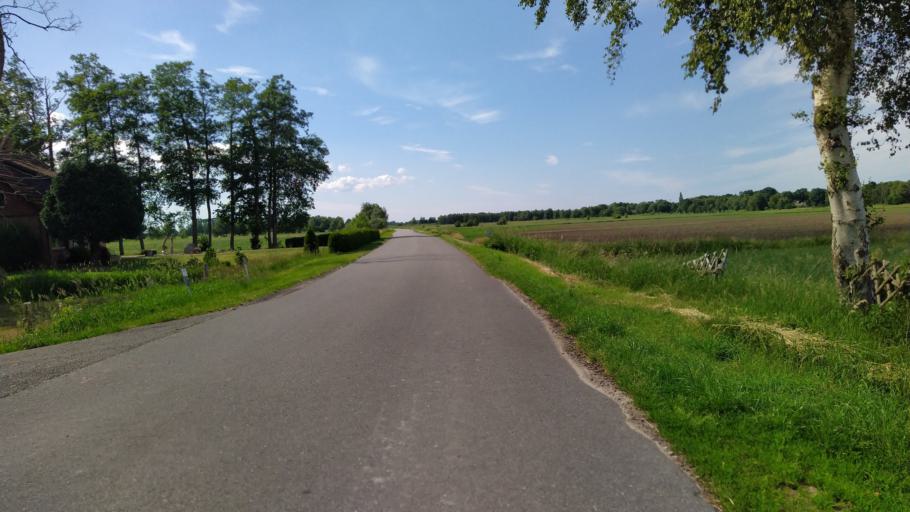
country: DE
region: Lower Saxony
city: Odisheim
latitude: 53.6650
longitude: 8.9286
